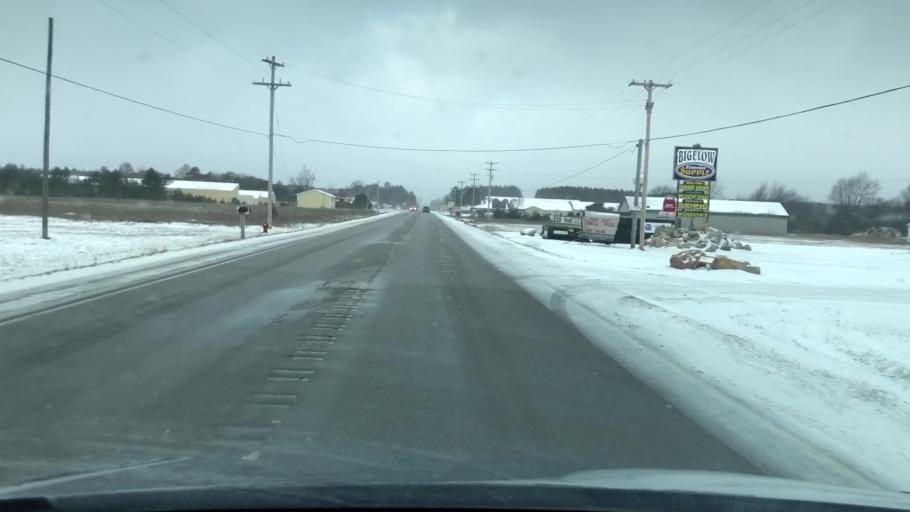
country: US
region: Michigan
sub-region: Wexford County
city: Cadillac
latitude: 44.2813
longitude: -85.4284
